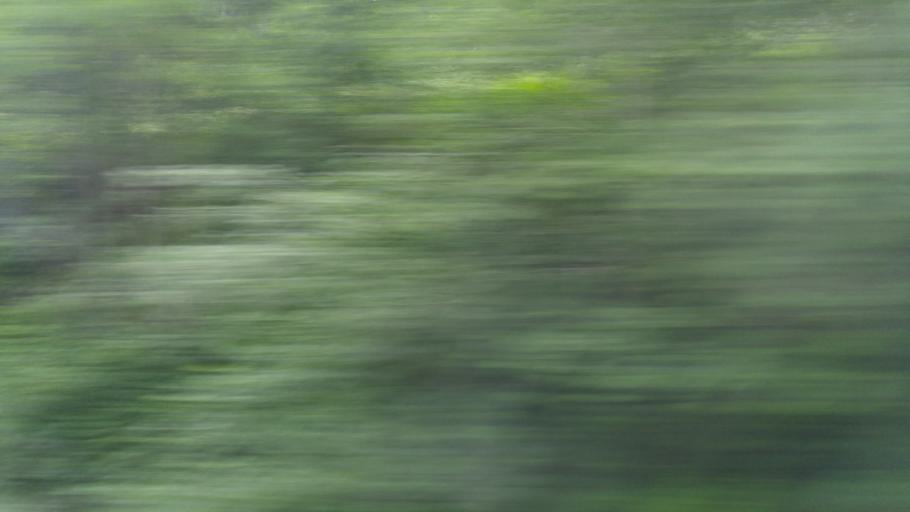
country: NO
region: Nord-Trondelag
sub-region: Levanger
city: Levanger
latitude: 63.4583
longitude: 11.3913
